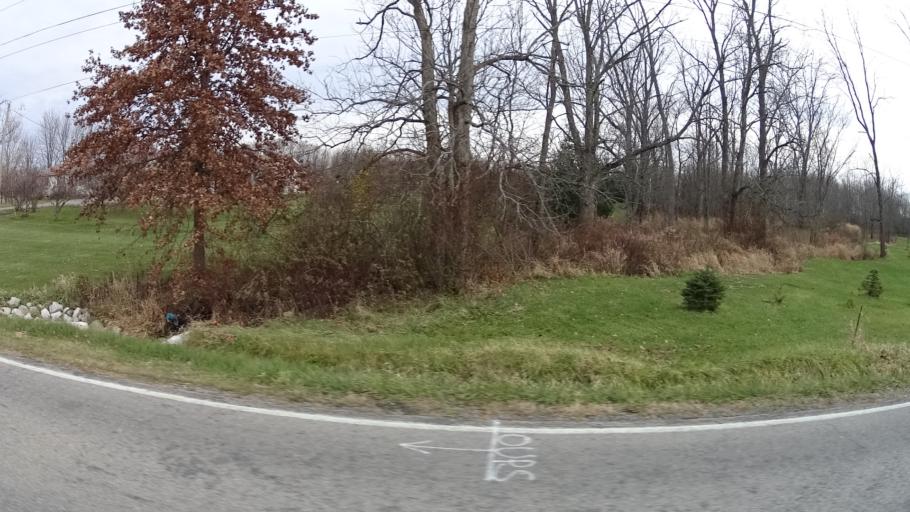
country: US
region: Ohio
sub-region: Lorain County
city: Lagrange
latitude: 41.1655
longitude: -82.0943
